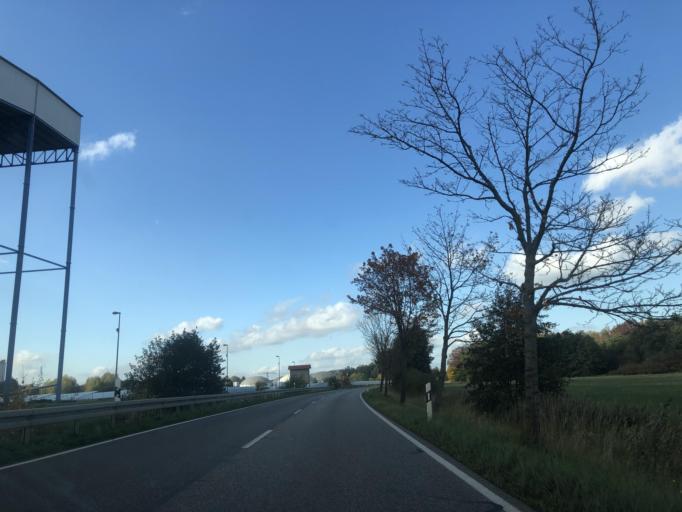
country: DE
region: Mecklenburg-Vorpommern
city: Wittenburg
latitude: 53.5095
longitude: 11.0939
